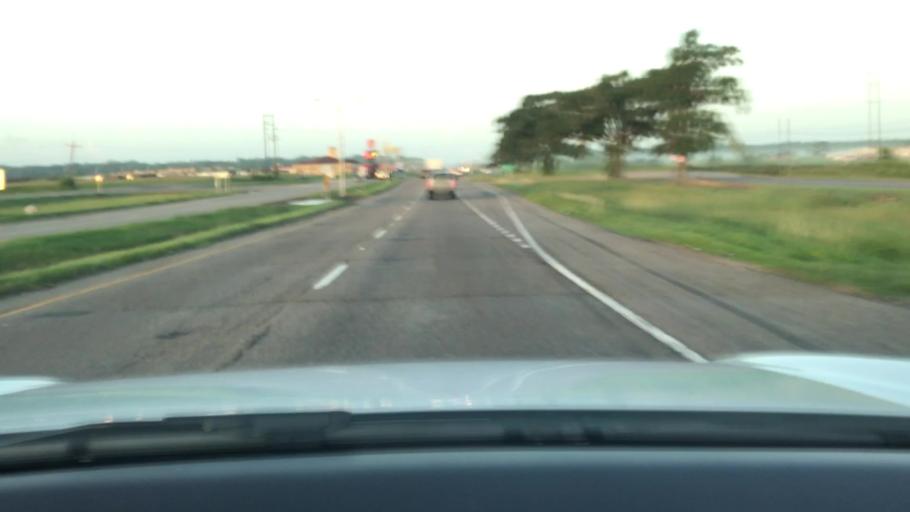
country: US
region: Louisiana
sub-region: West Baton Rouge Parish
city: Port Allen
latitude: 30.4288
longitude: -91.2137
